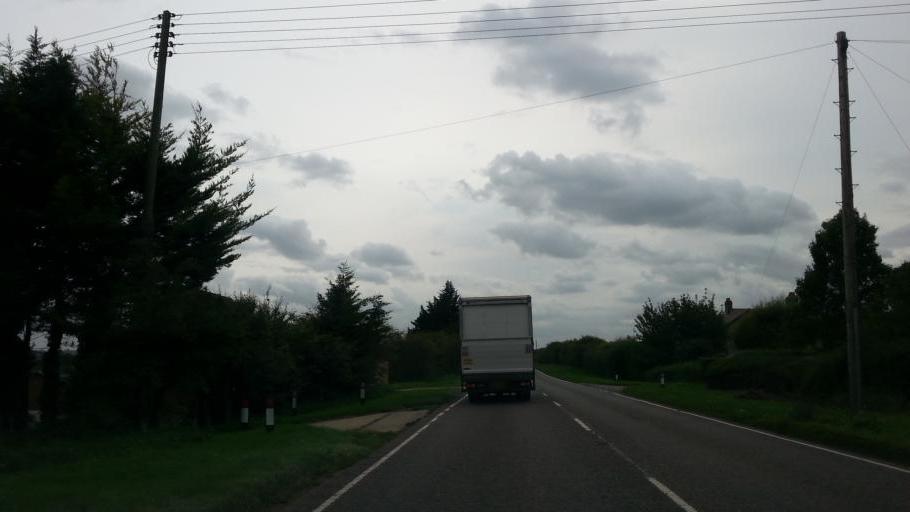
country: GB
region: England
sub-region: Cambridgeshire
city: Melbourn
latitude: 52.0547
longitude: 0.0227
